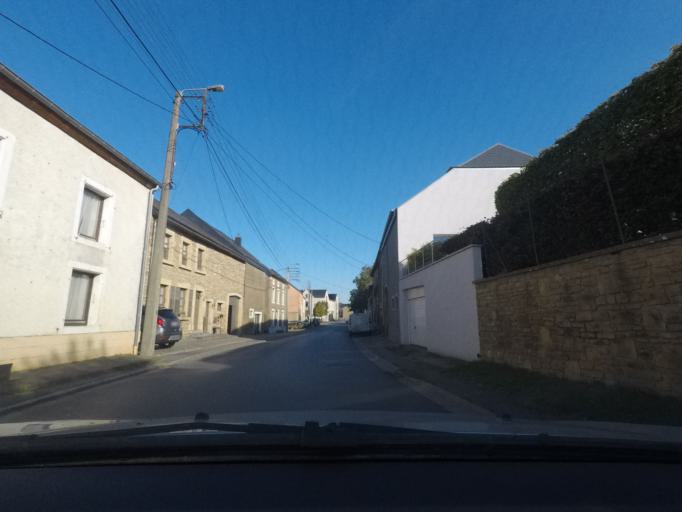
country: BE
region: Wallonia
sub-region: Province du Luxembourg
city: Messancy
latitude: 49.6295
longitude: 5.7992
